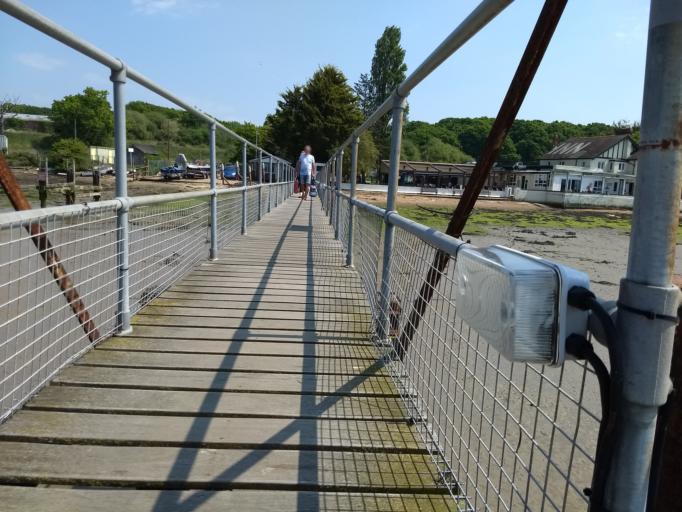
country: GB
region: England
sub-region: Isle of Wight
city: East Cowes
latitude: 50.7335
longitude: -1.2817
